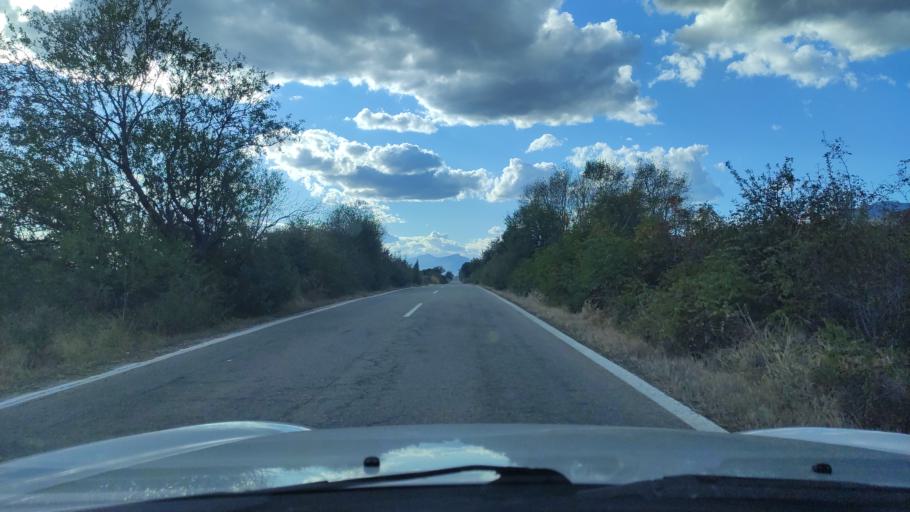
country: GR
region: East Macedonia and Thrace
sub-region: Nomos Rodopis
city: Iasmos
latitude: 41.1197
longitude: 25.0959
